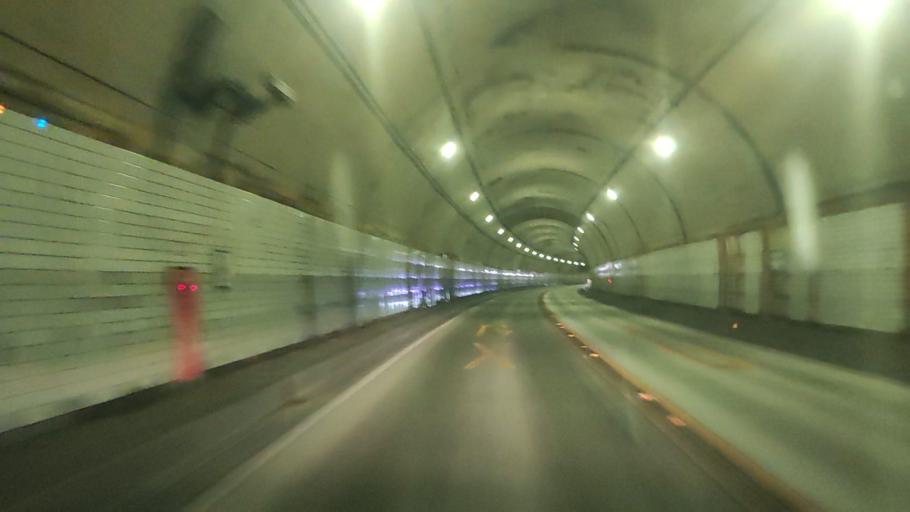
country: JP
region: Fukuoka
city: Maebaru-chuo
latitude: 33.4811
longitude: 130.2892
